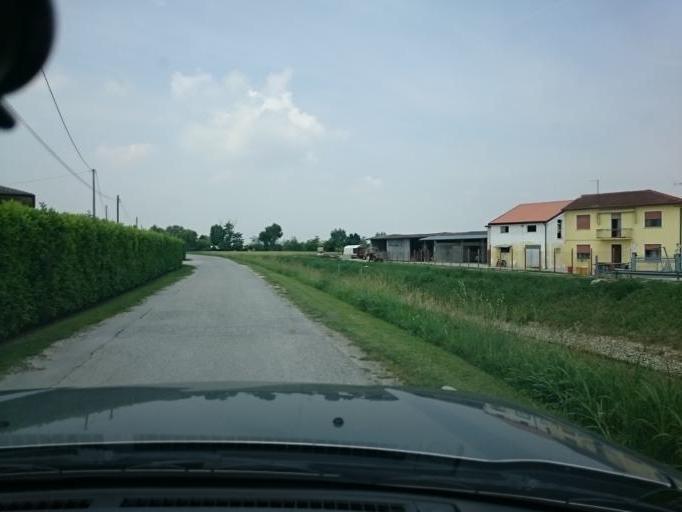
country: IT
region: Veneto
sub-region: Provincia di Padova
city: Codevigo
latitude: 45.2474
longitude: 12.0975
